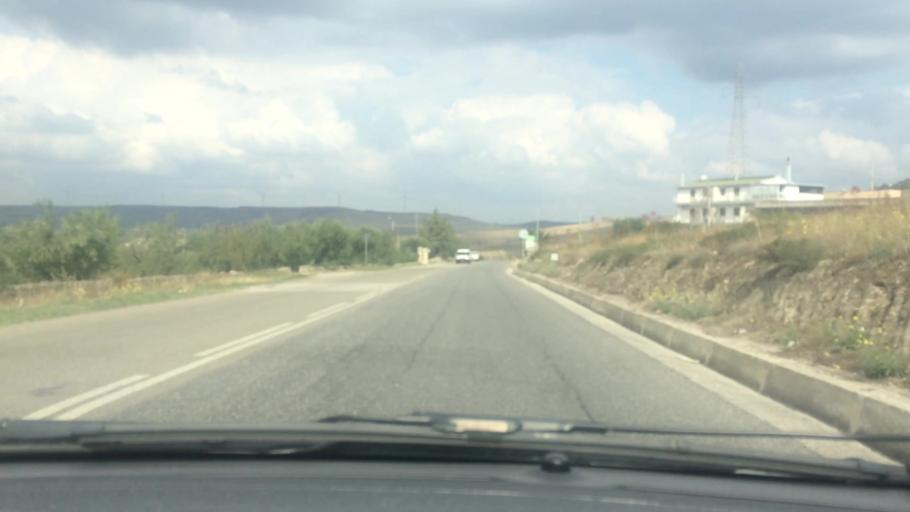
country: IT
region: Basilicate
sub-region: Provincia di Matera
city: Matera
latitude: 40.6849
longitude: 16.5704
